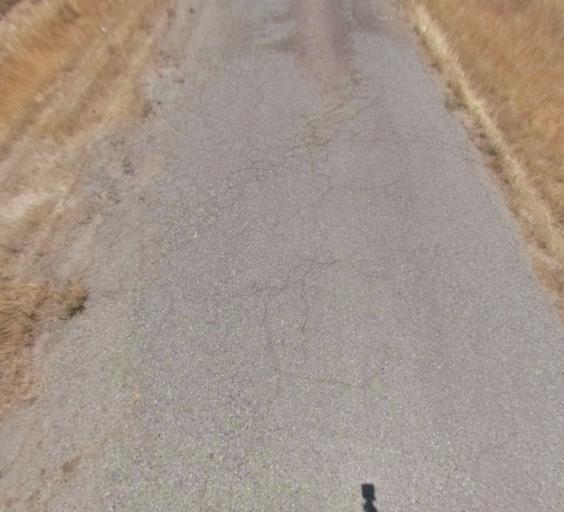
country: US
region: California
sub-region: Madera County
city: Bonadelle Ranchos-Madera Ranchos
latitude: 36.9583
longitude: -119.8306
